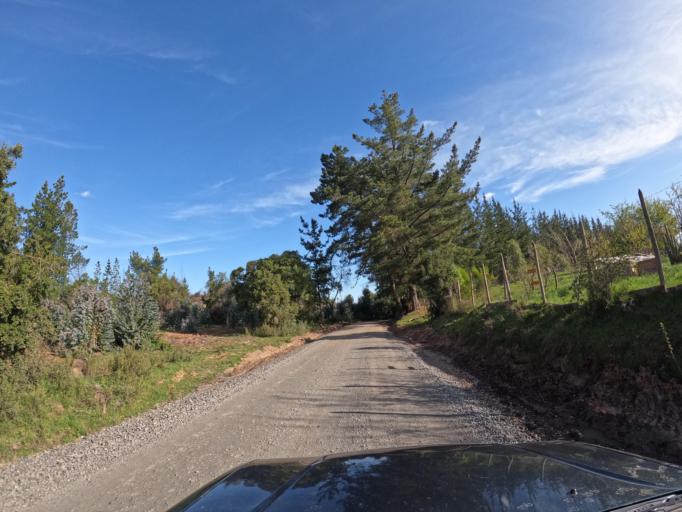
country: CL
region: Biobio
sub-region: Provincia de Biobio
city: La Laja
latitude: -37.1548
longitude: -72.7264
